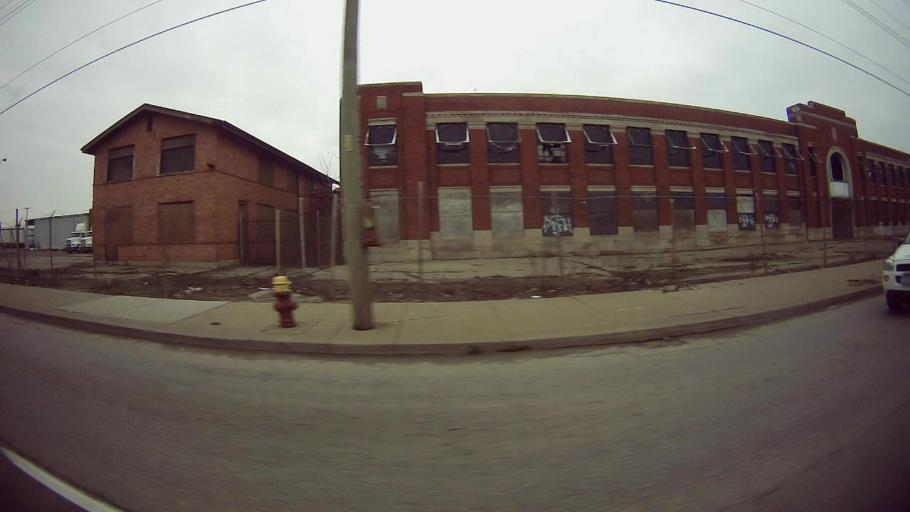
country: US
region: Michigan
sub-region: Wayne County
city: Hamtramck
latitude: 42.3811
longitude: -83.0356
